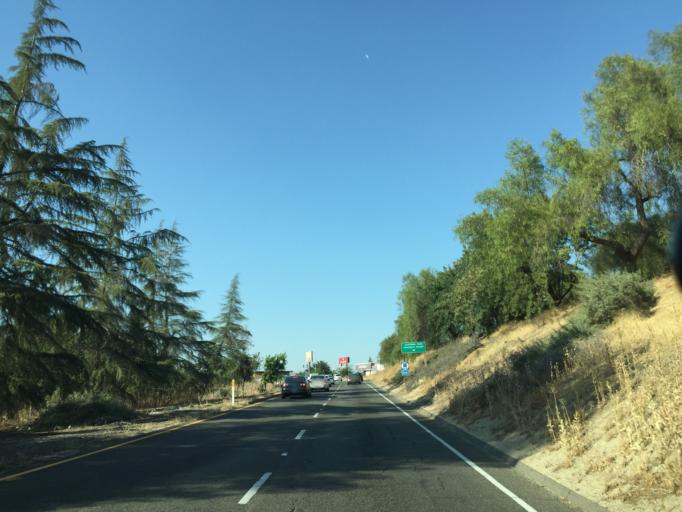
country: US
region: California
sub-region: Fresno County
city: Fresno
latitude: 36.8066
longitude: -119.7846
